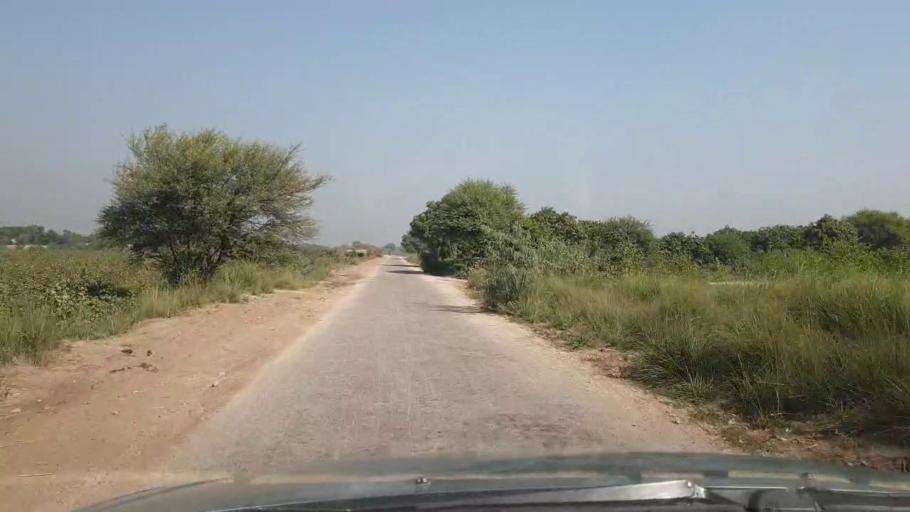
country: PK
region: Sindh
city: Tando Jam
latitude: 25.3151
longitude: 68.5399
